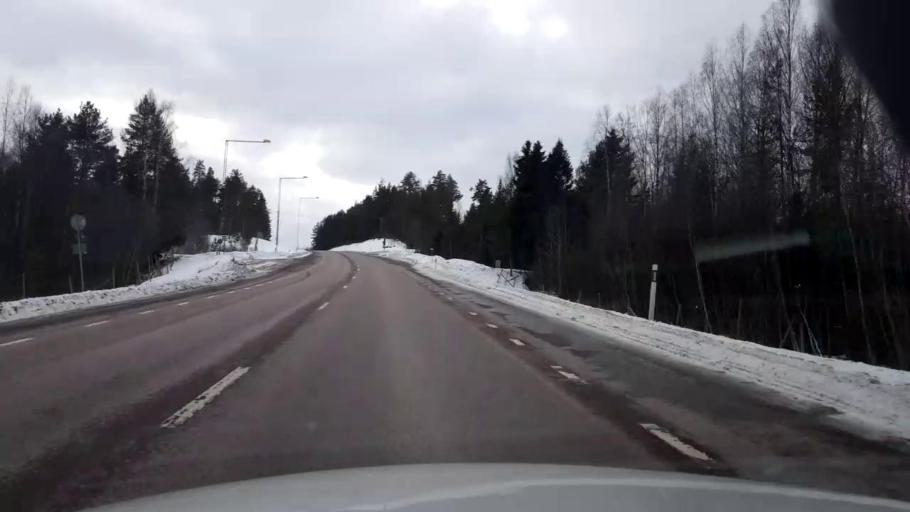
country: SE
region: Gaevleborg
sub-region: Nordanstigs Kommun
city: Bergsjoe
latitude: 61.9910
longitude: 17.2403
